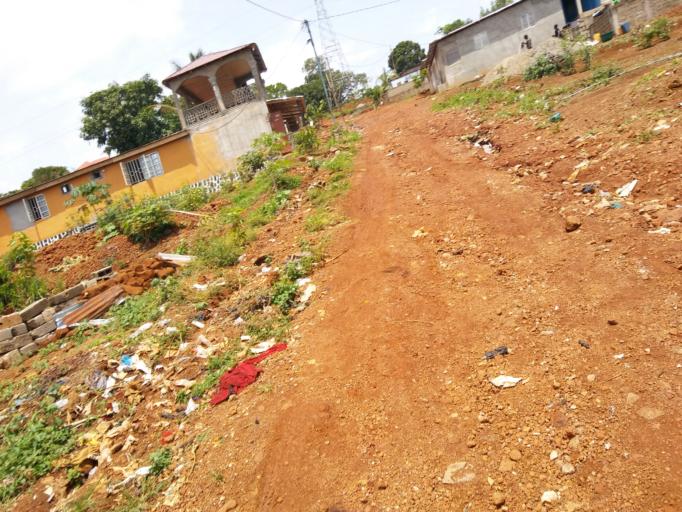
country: SL
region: Western Area
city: Hastings
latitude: 8.3899
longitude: -13.1594
